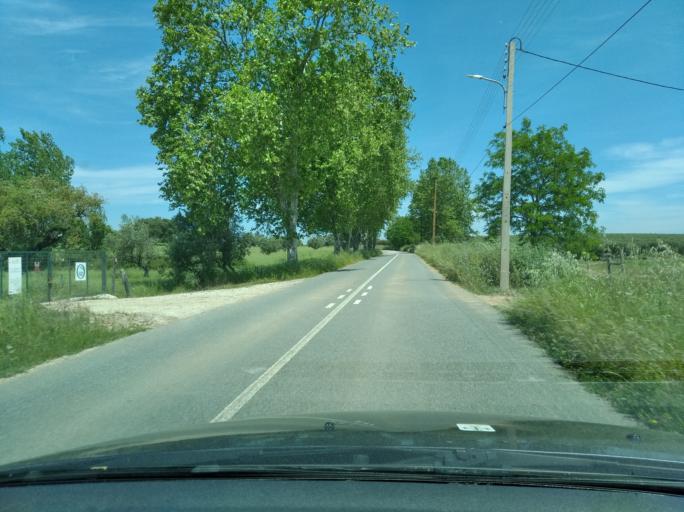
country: PT
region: Portalegre
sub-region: Avis
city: Avis
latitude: 39.0943
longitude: -7.8793
